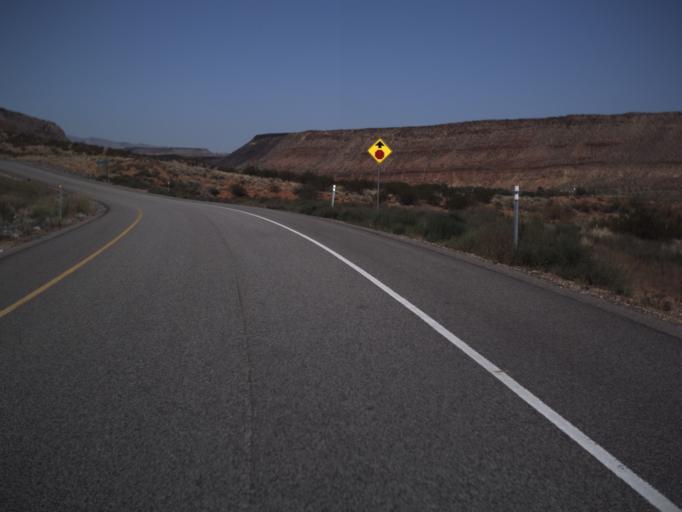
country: US
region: Utah
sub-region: Washington County
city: Washington
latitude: 37.1145
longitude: -113.4483
